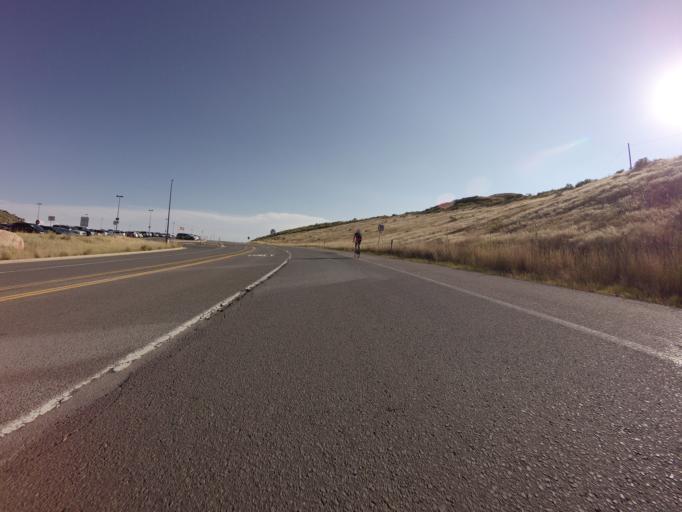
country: US
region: Colorado
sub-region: Jefferson County
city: West Pleasant View
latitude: 39.7006
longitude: -105.2067
